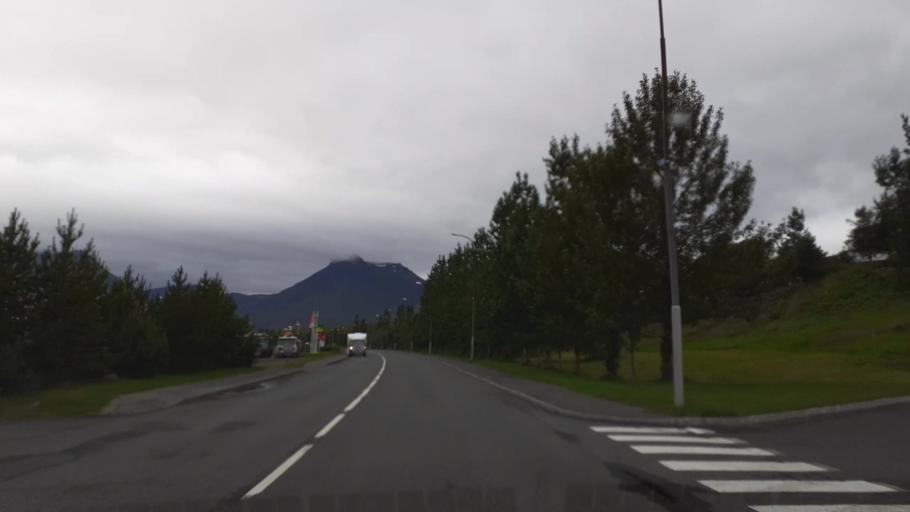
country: IS
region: East
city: Reydarfjoerdur
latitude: 65.0344
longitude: -14.2282
